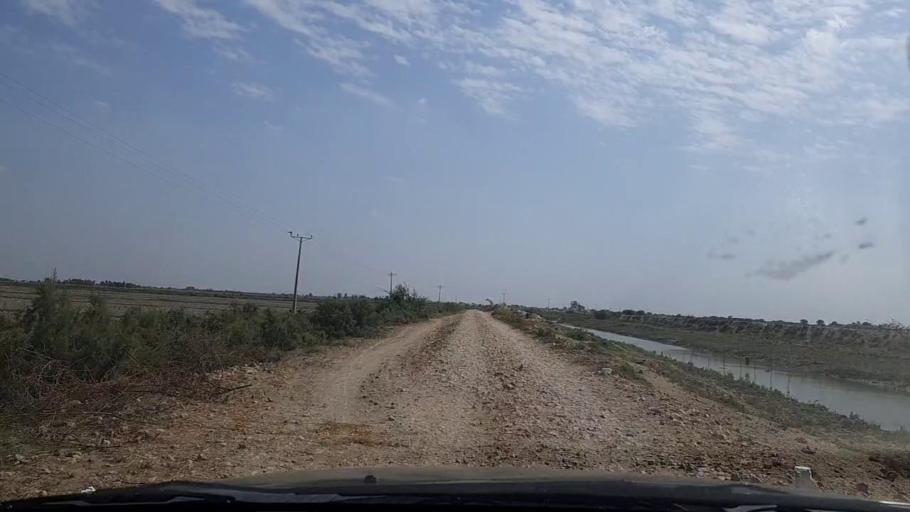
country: PK
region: Sindh
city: Mirpur Batoro
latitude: 24.5934
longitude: 68.1974
